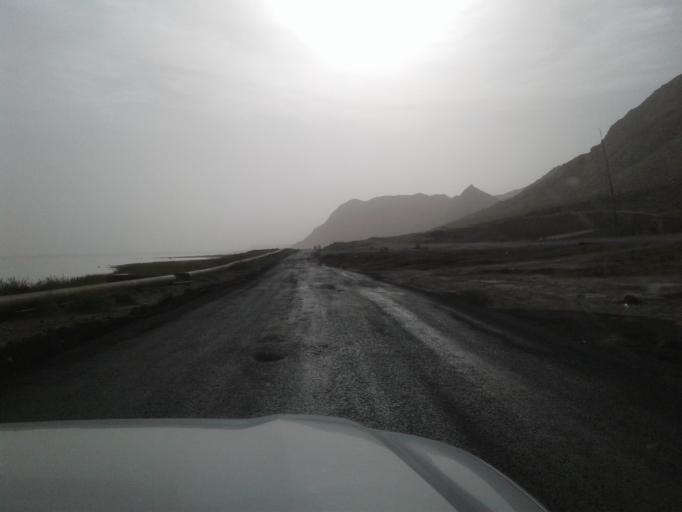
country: TM
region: Balkan
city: Turkmenbasy
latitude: 40.0323
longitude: 52.9269
